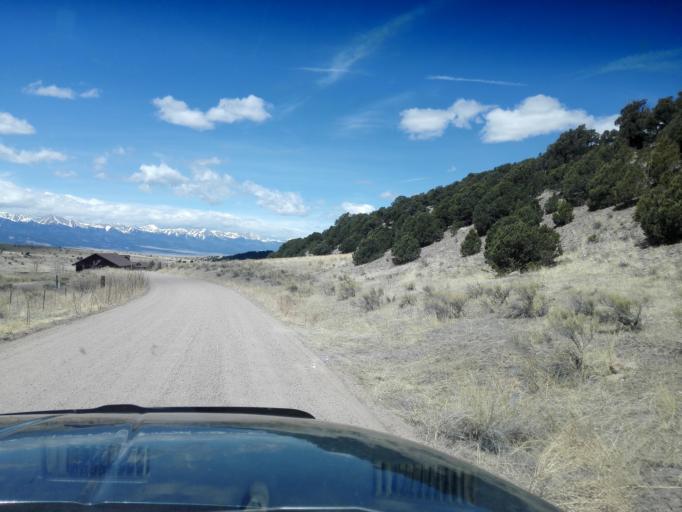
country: US
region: Colorado
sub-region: Custer County
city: Westcliffe
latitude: 37.9767
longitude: -105.2931
